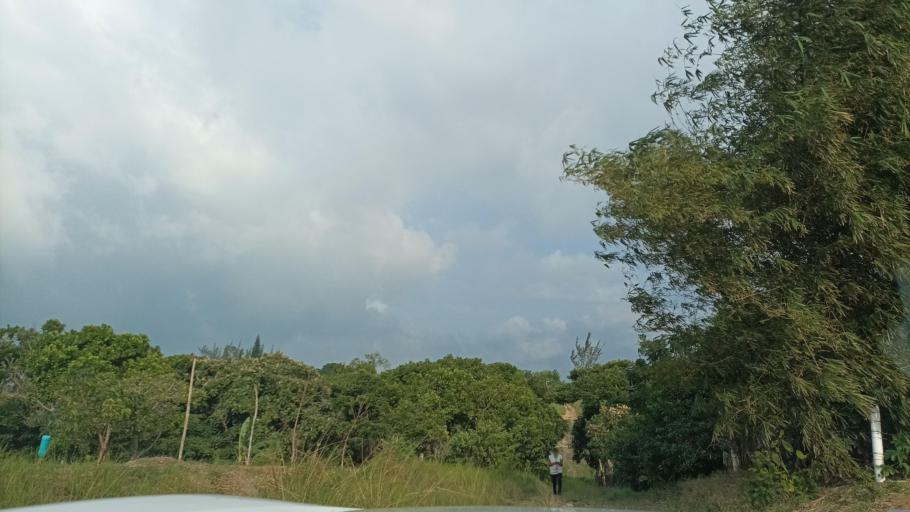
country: MX
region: Veracruz
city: Allende
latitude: 18.1568
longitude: -94.3272
